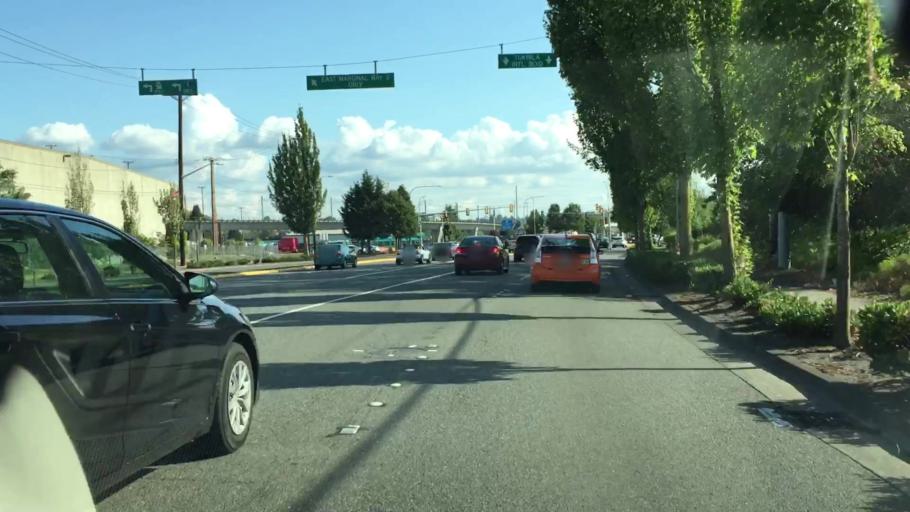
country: US
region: Washington
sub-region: King County
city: Riverton
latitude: 47.5086
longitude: -122.2917
